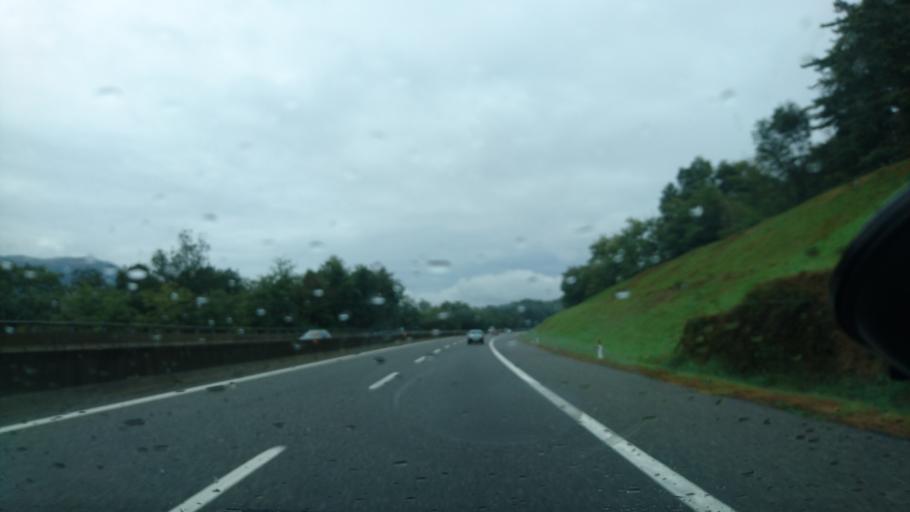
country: IT
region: Piedmont
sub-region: Provincia di Novara
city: Pisano
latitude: 45.7875
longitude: 8.5139
